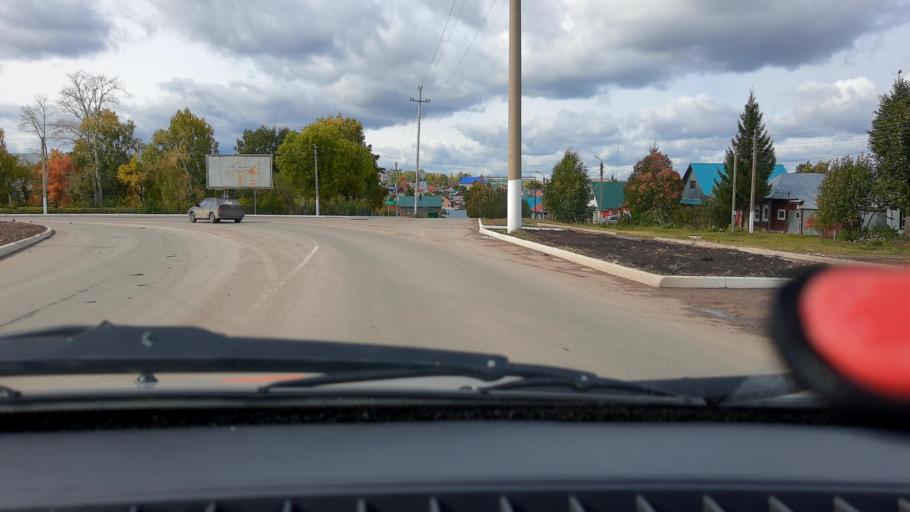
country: RU
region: Bashkortostan
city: Belebey
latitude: 54.1011
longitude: 54.1206
